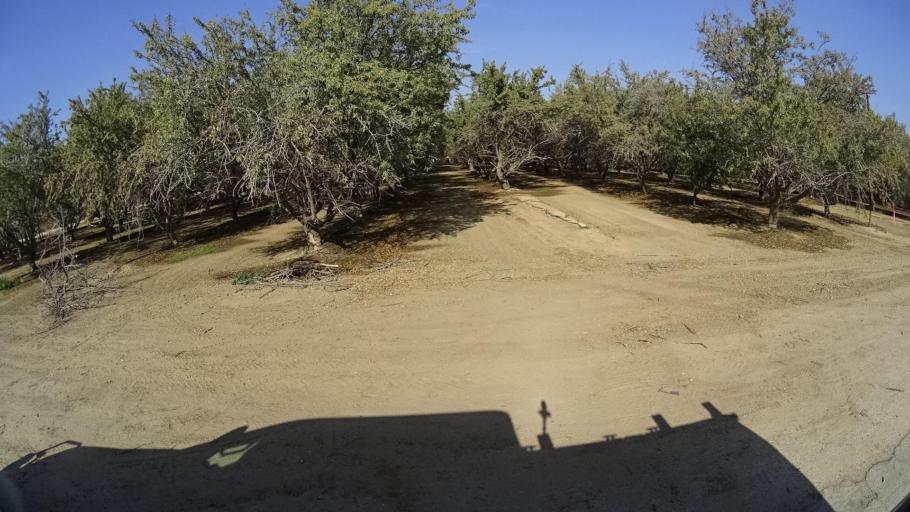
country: US
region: California
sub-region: Kern County
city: Shafter
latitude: 35.5442
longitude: -119.1418
